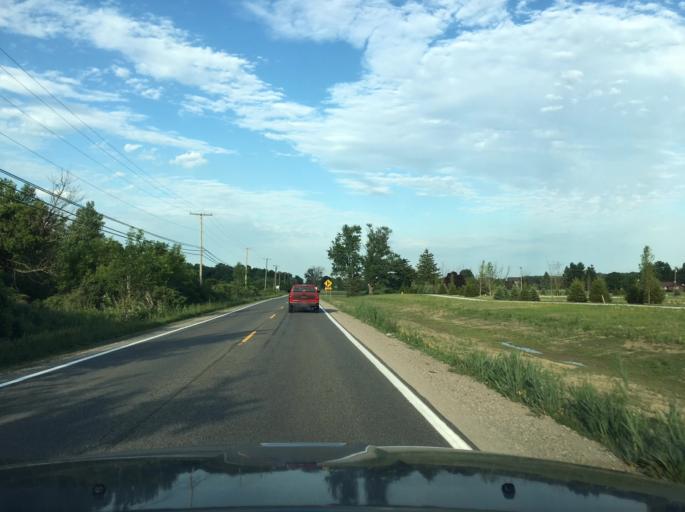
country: US
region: Michigan
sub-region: Macomb County
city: Shelby
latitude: 42.7165
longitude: -82.9426
